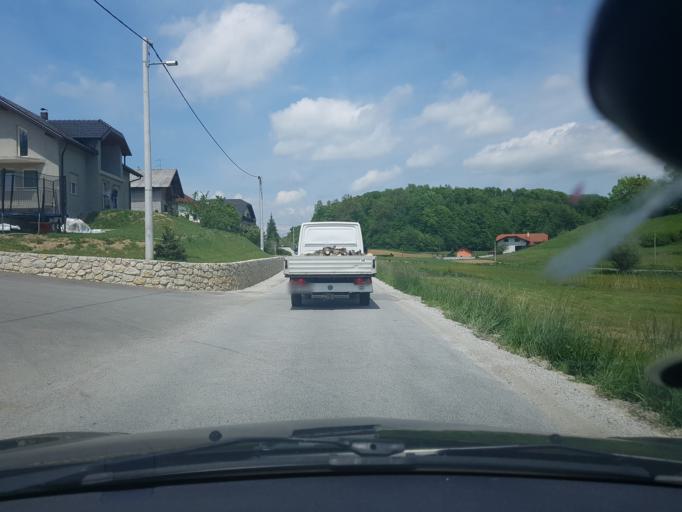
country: SI
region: Rogatec
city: Rogatec
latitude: 46.2033
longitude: 15.7325
